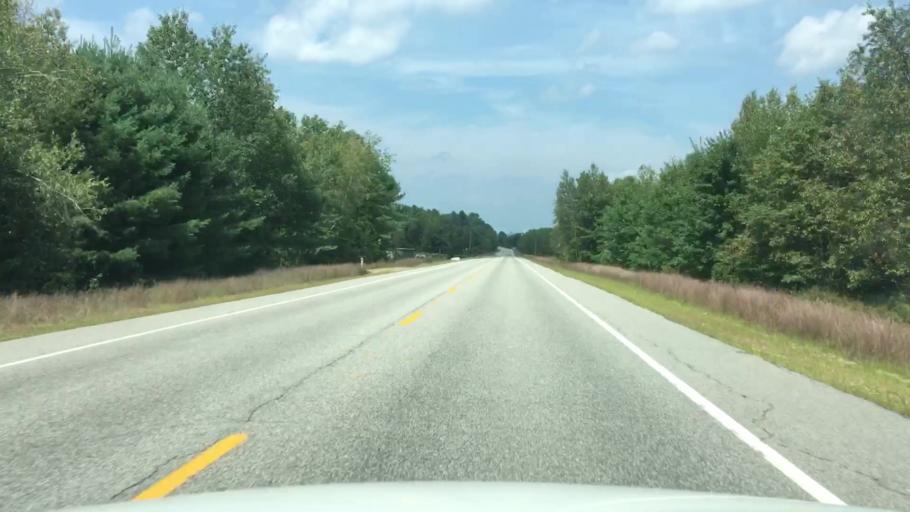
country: US
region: Maine
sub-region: Oxford County
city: Canton
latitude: 44.4255
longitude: -70.2970
